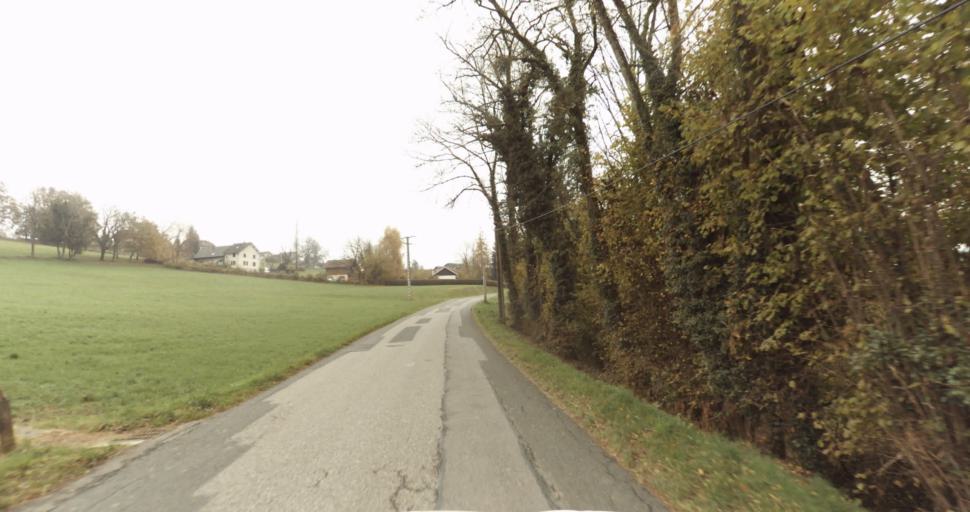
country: FR
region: Rhone-Alpes
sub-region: Departement de la Haute-Savoie
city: Gruffy
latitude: 45.7991
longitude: 6.0352
